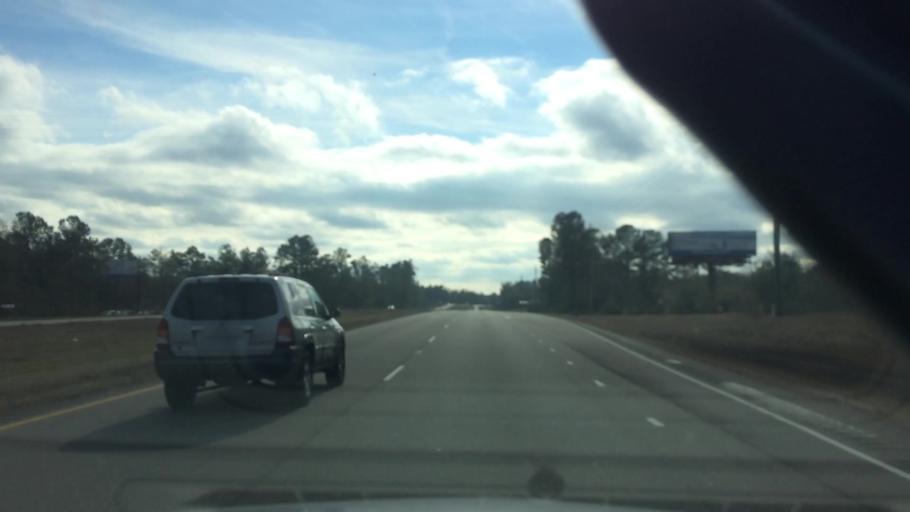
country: US
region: North Carolina
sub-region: Brunswick County
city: Bolivia
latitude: 34.1255
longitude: -78.1044
